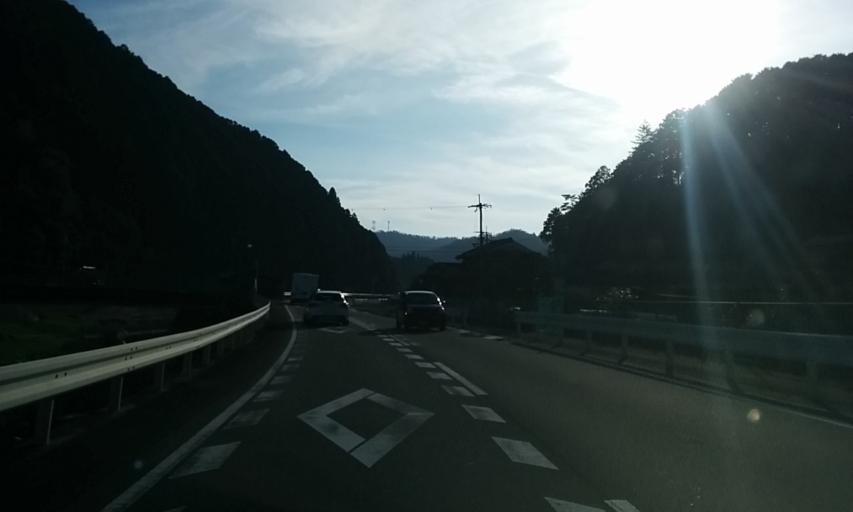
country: JP
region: Kyoto
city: Kameoka
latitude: 35.1901
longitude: 135.5203
